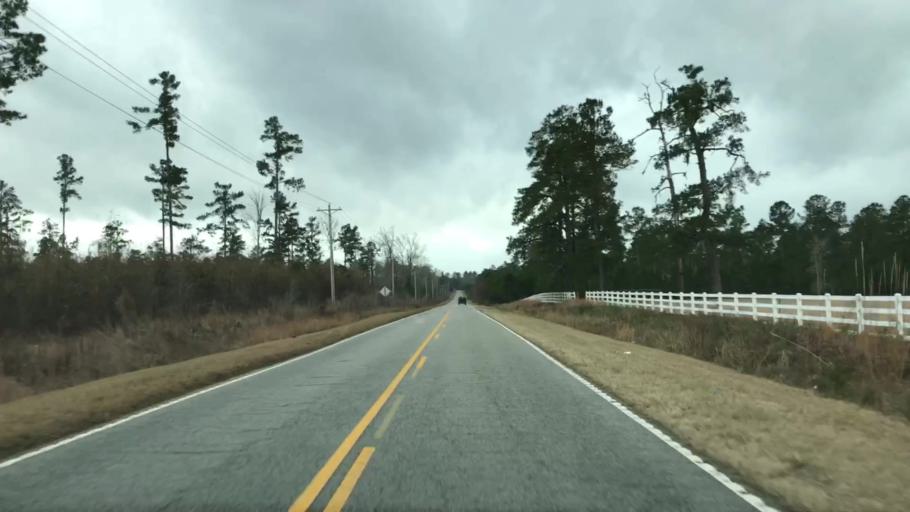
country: US
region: South Carolina
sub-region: Florence County
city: Johnsonville
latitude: 33.6476
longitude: -79.4202
